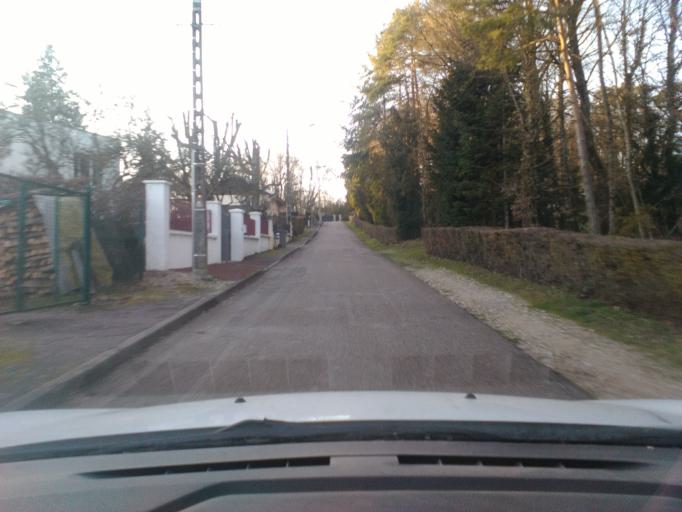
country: FR
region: Lorraine
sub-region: Departement des Vosges
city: Mirecourt
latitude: 48.2970
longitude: 6.1235
